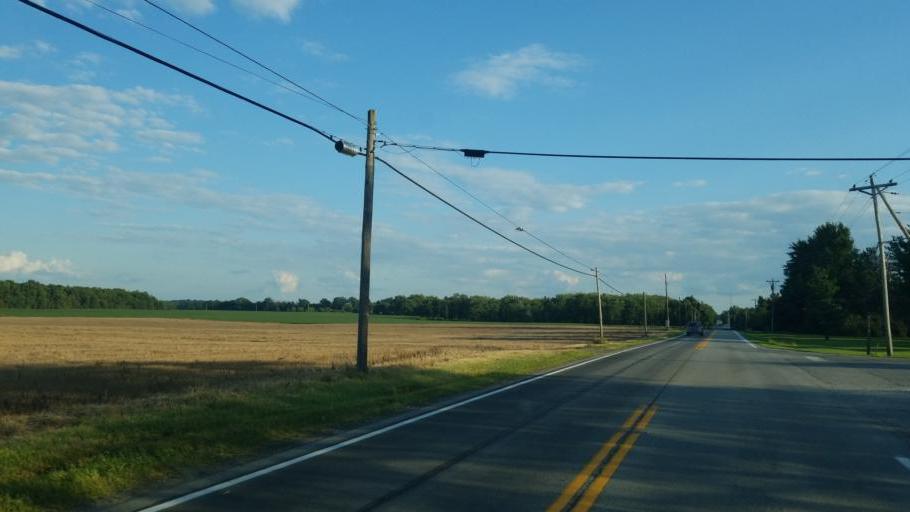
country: US
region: Ohio
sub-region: Huron County
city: Willard
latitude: 41.0863
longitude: -82.7182
